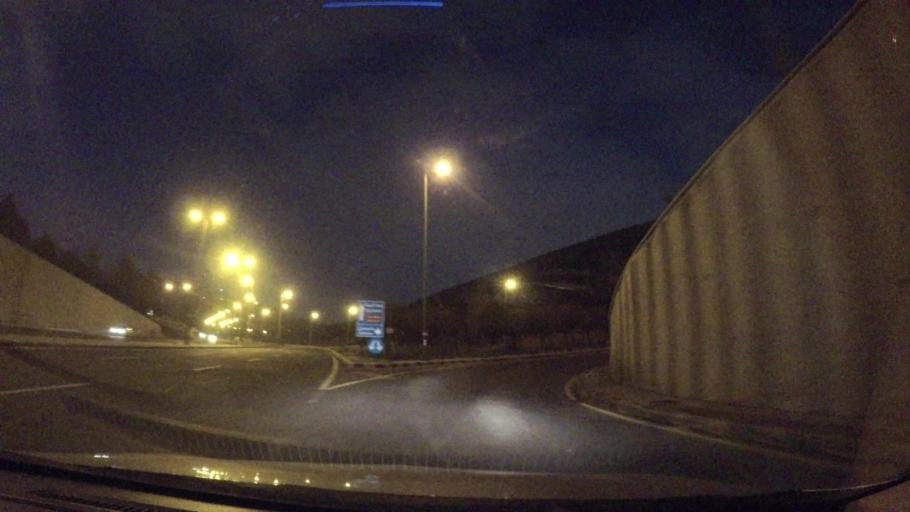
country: JO
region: Amman
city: Al Bunayyat ash Shamaliyah
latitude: 31.9293
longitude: 35.8840
